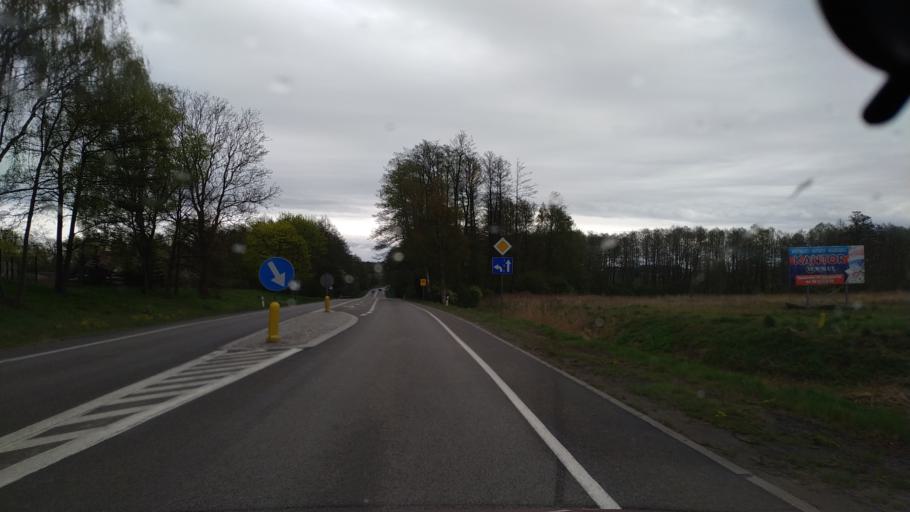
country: PL
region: Pomeranian Voivodeship
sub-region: Powiat starogardzki
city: Zblewo
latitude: 53.9309
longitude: 18.3273
